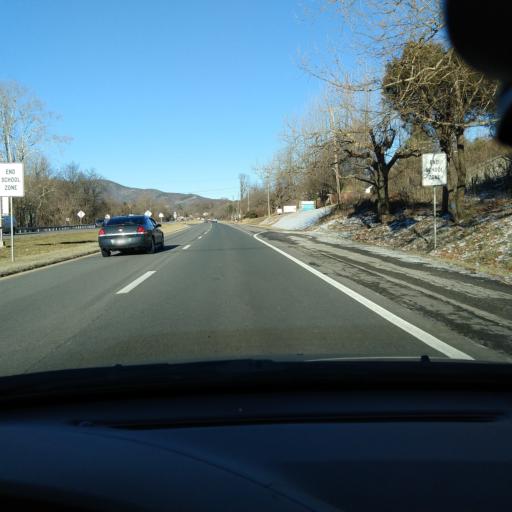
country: US
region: Virginia
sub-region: Botetourt County
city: Blue Ridge
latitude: 37.3677
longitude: -79.8154
